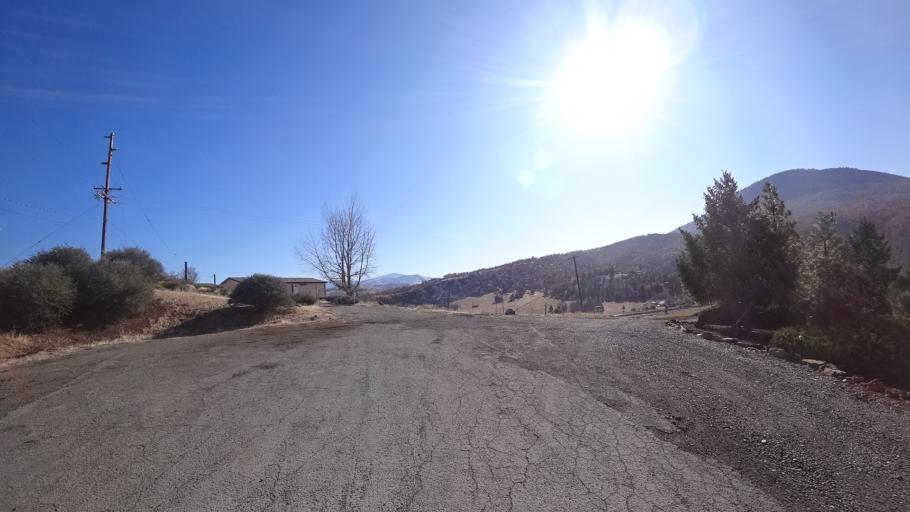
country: US
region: California
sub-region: Siskiyou County
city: Montague
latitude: 41.8992
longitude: -122.5211
